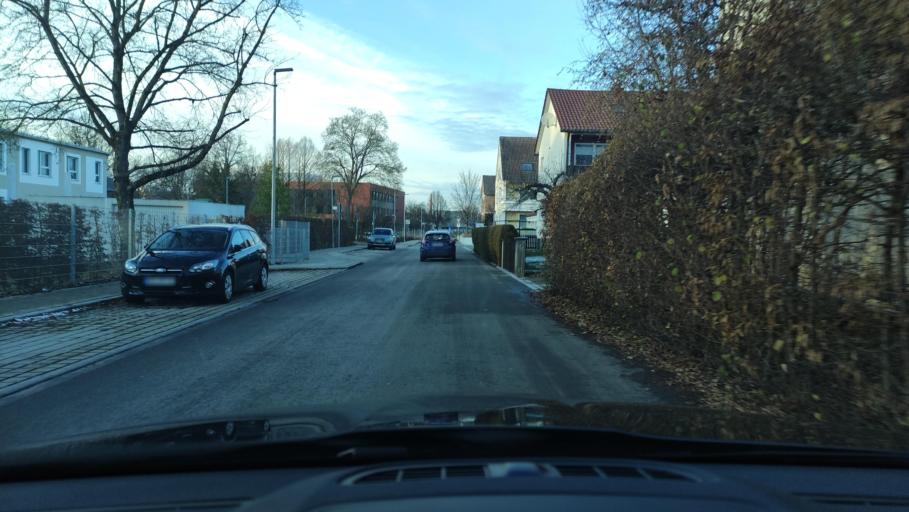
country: DE
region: Bavaria
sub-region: Swabia
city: Krumbach
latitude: 48.2468
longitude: 10.3645
